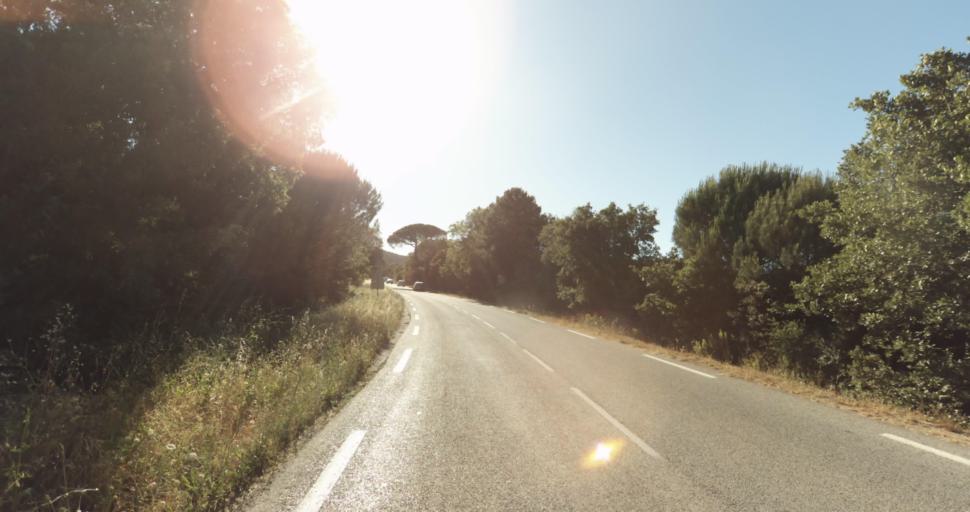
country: FR
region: Provence-Alpes-Cote d'Azur
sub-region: Departement du Var
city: Ramatuelle
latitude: 43.2386
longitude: 6.6051
